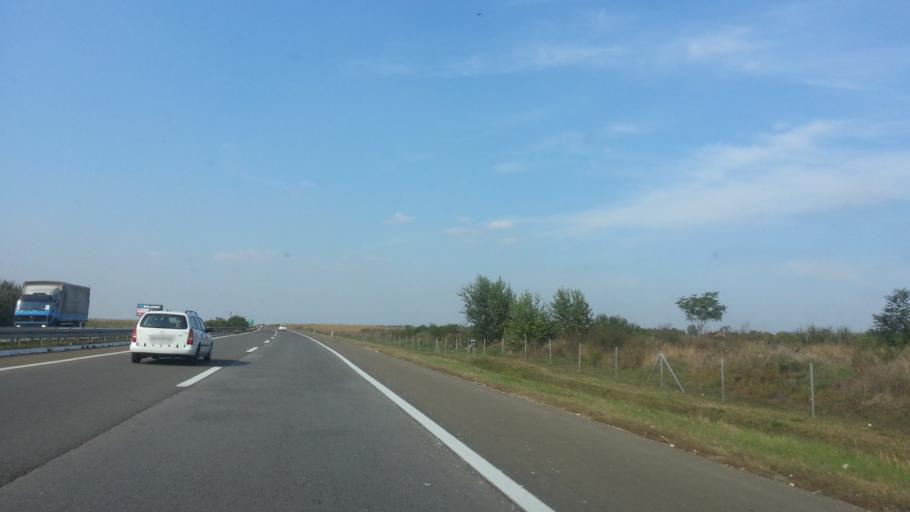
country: RS
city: Novi Banovci
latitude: 44.9173
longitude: 20.3052
